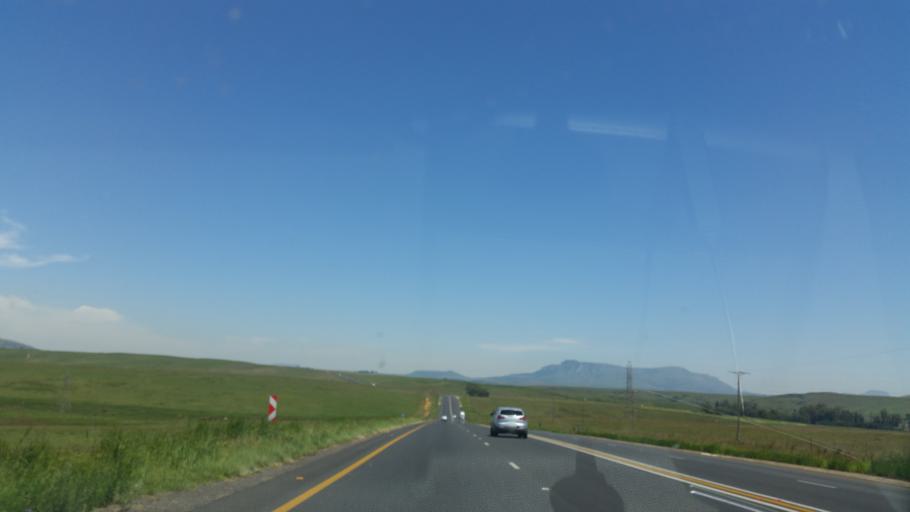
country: ZA
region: Orange Free State
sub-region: Thabo Mofutsanyana District Municipality
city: Harrismith
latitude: -28.3698
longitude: 29.3667
